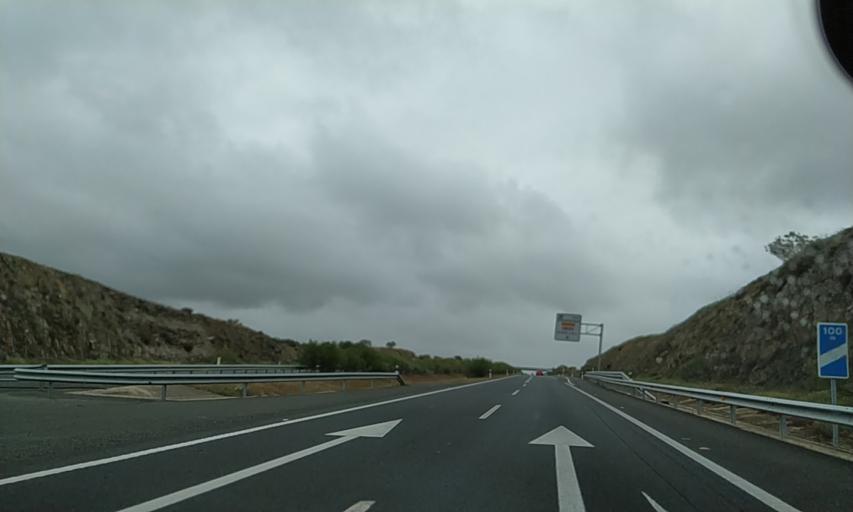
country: ES
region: Extremadura
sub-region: Provincia de Caceres
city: Hinojal
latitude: 39.7034
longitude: -6.4052
